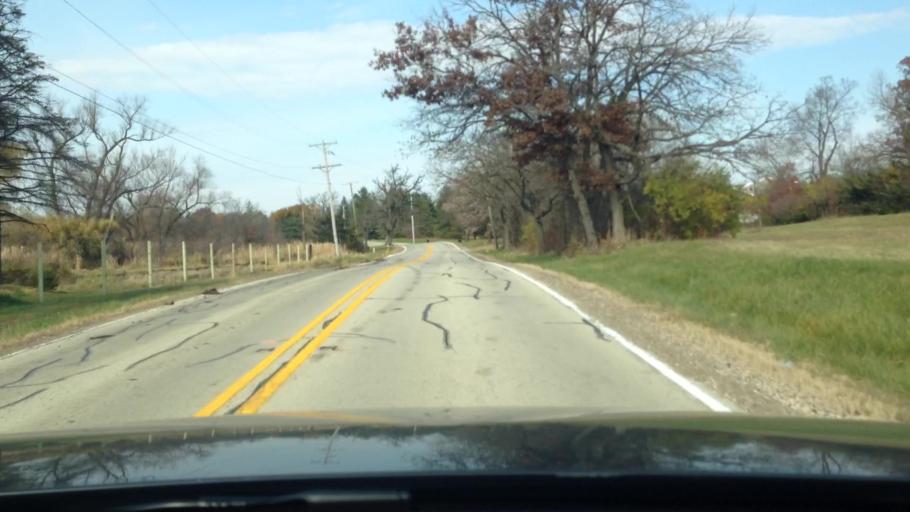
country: US
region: Illinois
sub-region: McHenry County
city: Woodstock
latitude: 42.2577
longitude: -88.4476
